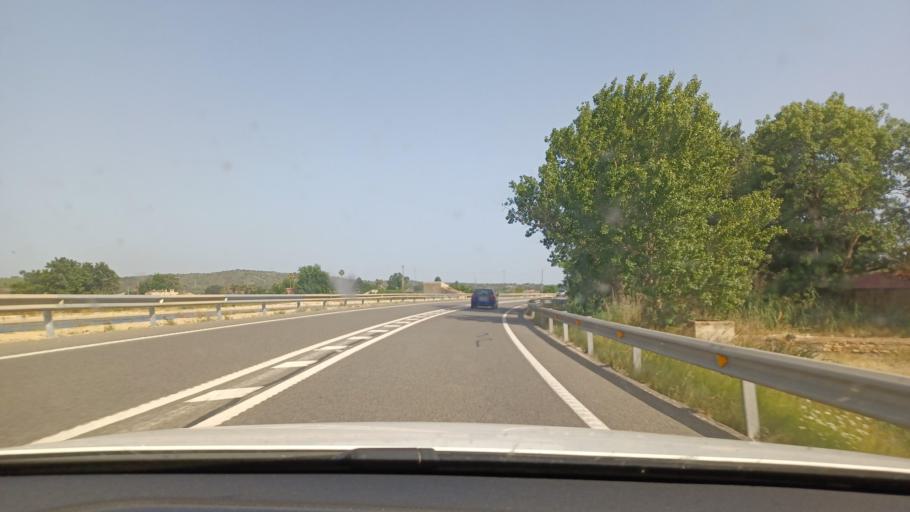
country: ES
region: Catalonia
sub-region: Provincia de Tarragona
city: Amposta
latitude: 40.7471
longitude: 0.5579
